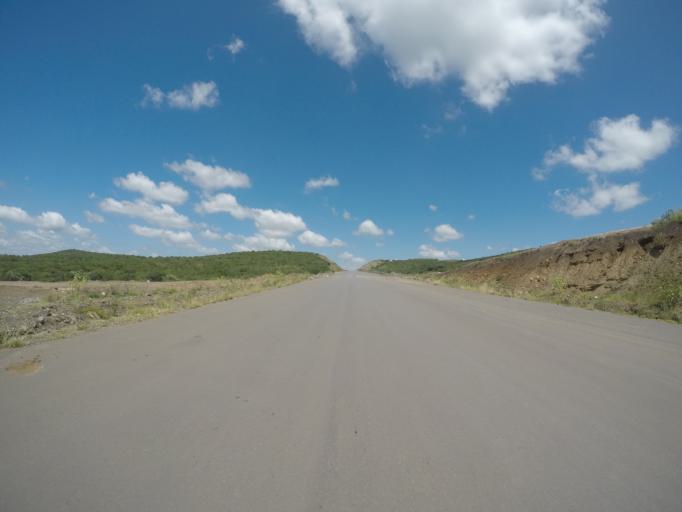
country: ZA
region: KwaZulu-Natal
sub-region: uThungulu District Municipality
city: Empangeni
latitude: -28.6233
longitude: 31.7575
